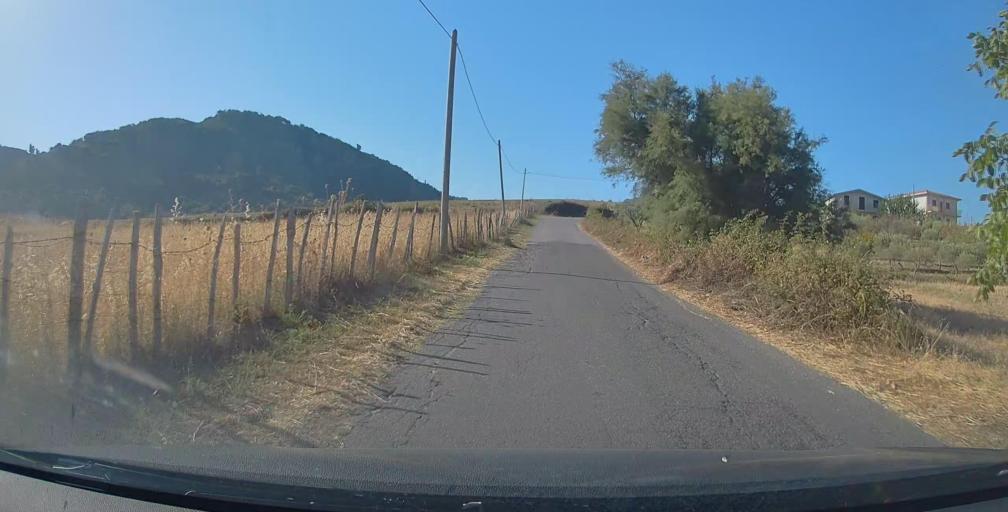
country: IT
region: Sicily
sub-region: Messina
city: San Piero Patti
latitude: 38.0706
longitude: 14.9862
